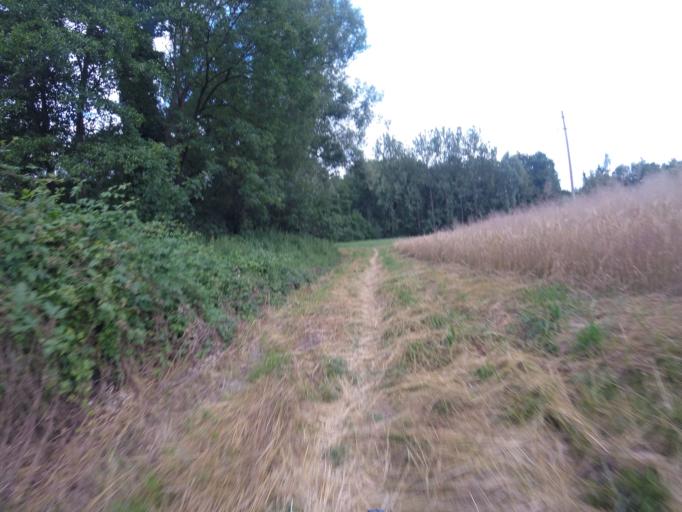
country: DE
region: Baden-Wuerttemberg
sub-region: Regierungsbezirk Stuttgart
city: Oppenweiler
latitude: 48.9637
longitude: 9.4648
